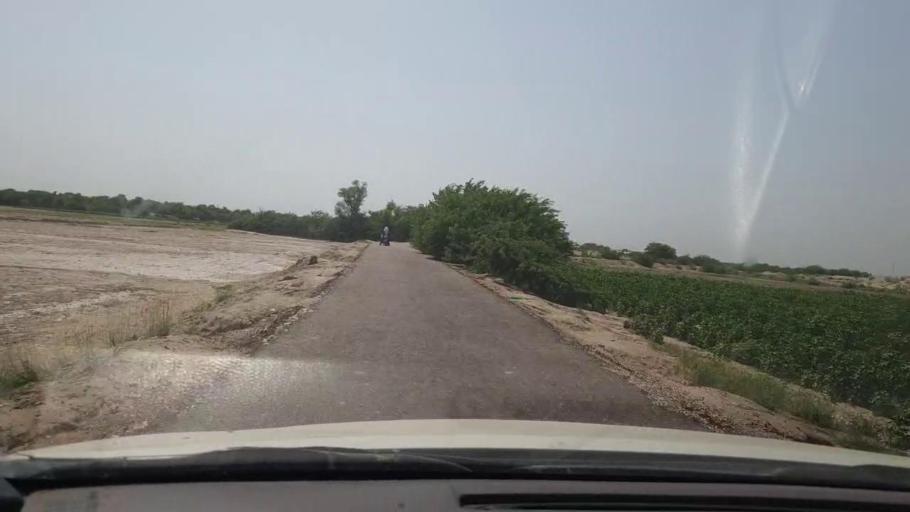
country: PK
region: Sindh
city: Rohri
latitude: 27.5184
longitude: 69.0774
